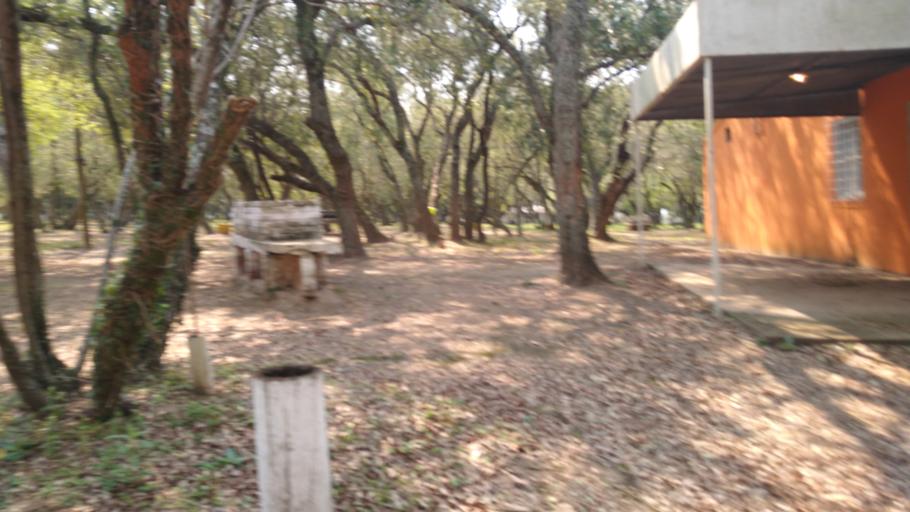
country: AR
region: Corrientes
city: Ituzaingo
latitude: -27.5471
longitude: -56.6745
